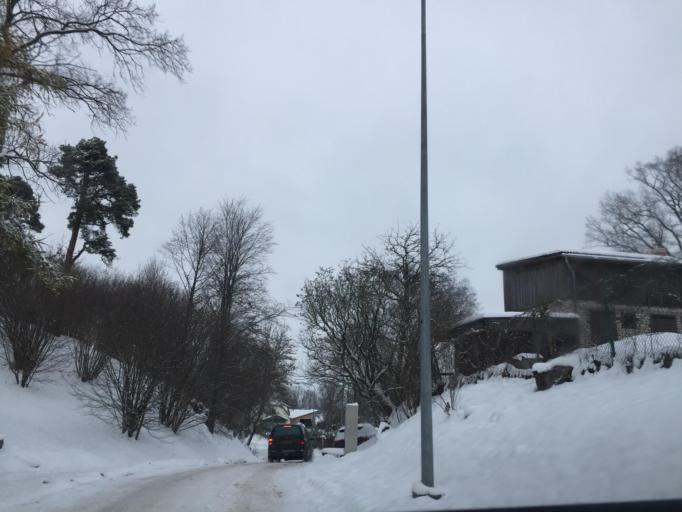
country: LV
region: Smiltene
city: Smiltene
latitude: 57.4200
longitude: 25.8985
